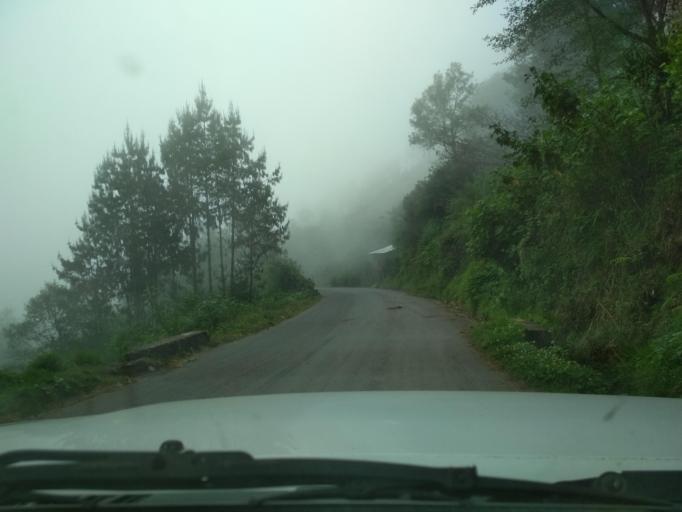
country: MX
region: Veracruz
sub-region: La Perla
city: Chilapa
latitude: 18.9697
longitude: -97.1728
